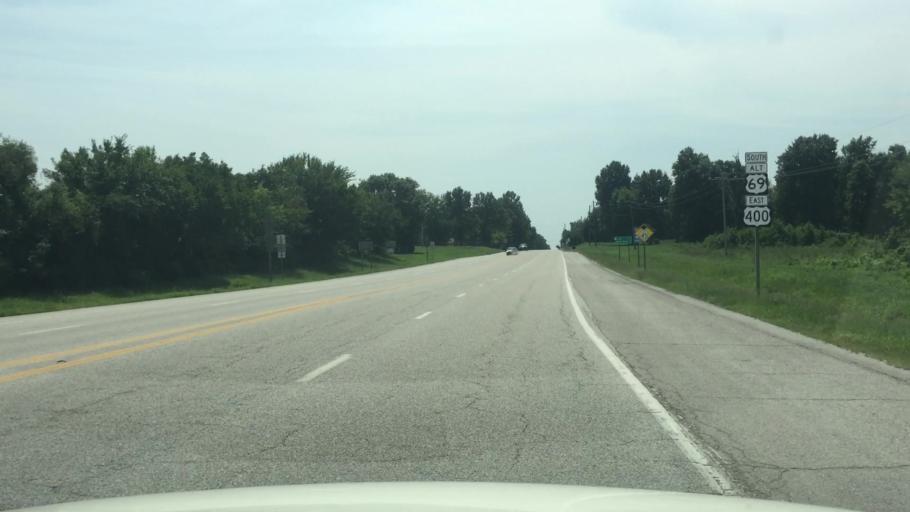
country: US
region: Kansas
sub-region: Cherokee County
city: Galena
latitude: 37.1763
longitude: -94.7045
